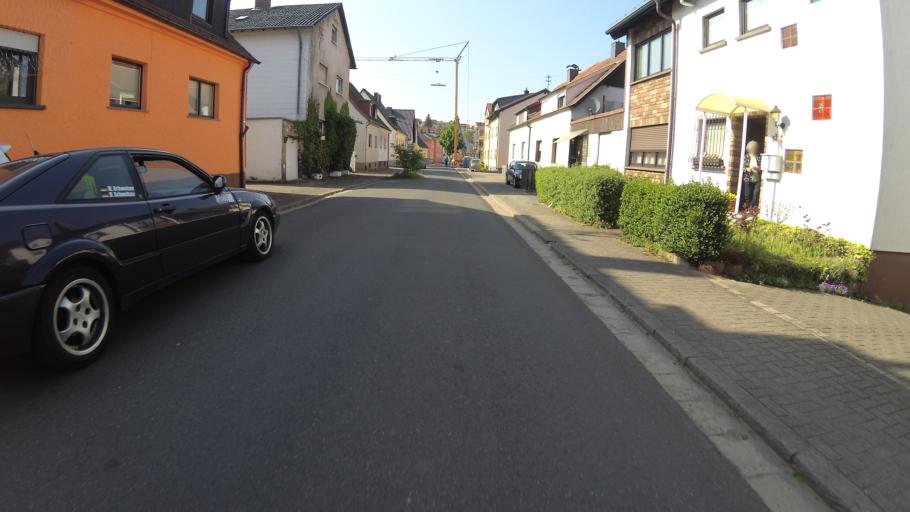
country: DE
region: Saarland
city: Illingen
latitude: 49.3719
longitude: 7.0482
